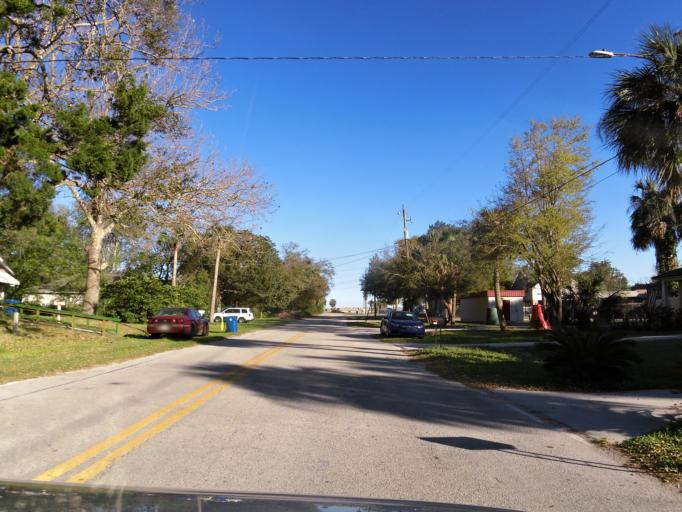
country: US
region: Florida
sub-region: Duval County
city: Atlantic Beach
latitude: 30.3946
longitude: -81.4283
